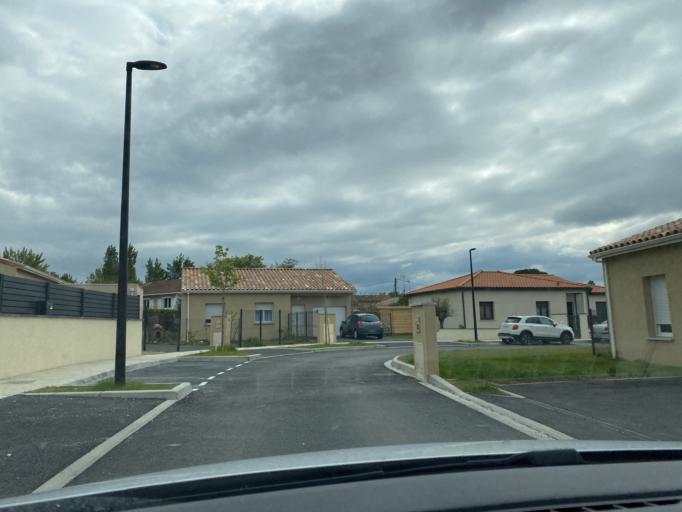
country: FR
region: Midi-Pyrenees
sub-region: Departement de la Haute-Garonne
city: Ayguesvives
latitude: 43.4282
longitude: 1.5947
